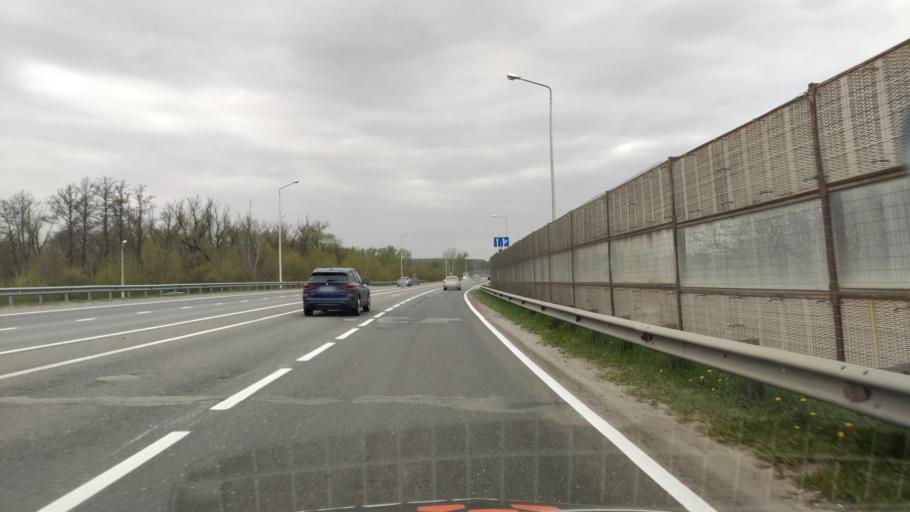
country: RU
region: Belgorod
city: Staryy Oskol
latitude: 51.3467
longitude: 37.8222
